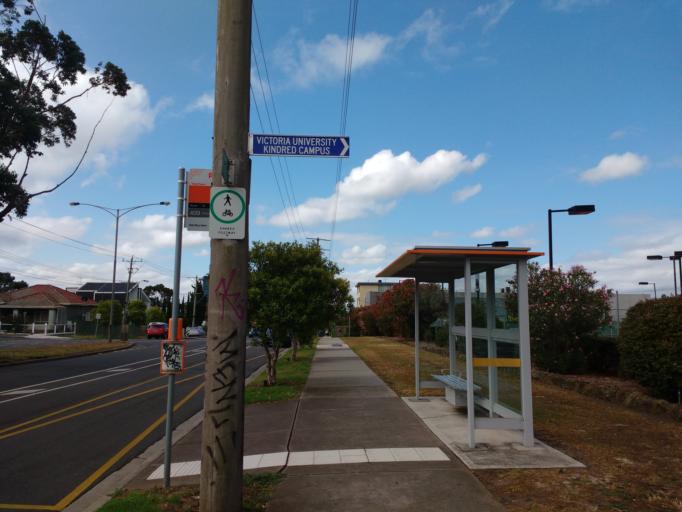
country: AU
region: Victoria
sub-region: Maribyrnong
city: Yarraville
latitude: -37.8112
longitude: 144.8985
